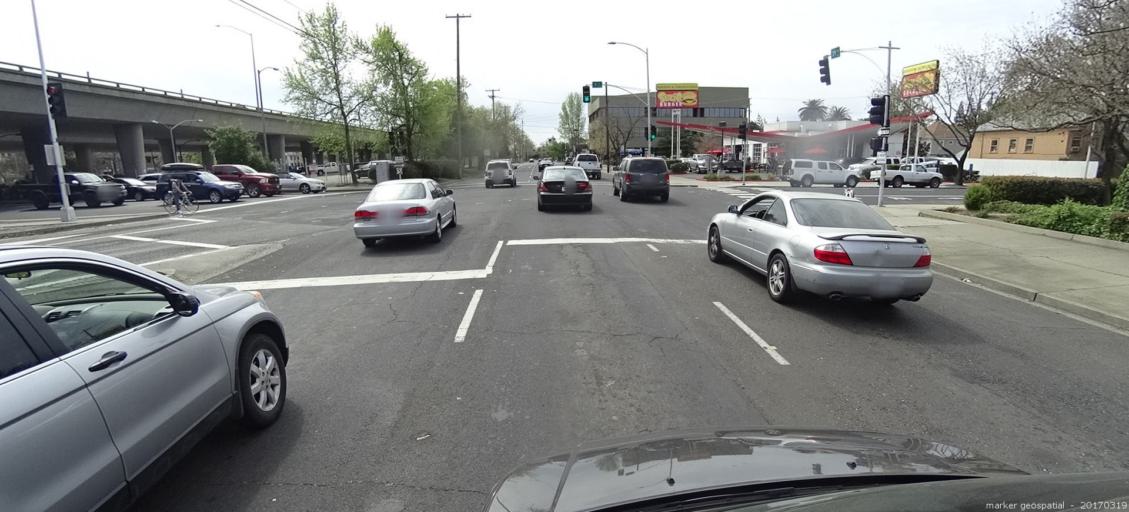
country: US
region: California
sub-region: Sacramento County
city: Sacramento
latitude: 38.5671
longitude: -121.4707
